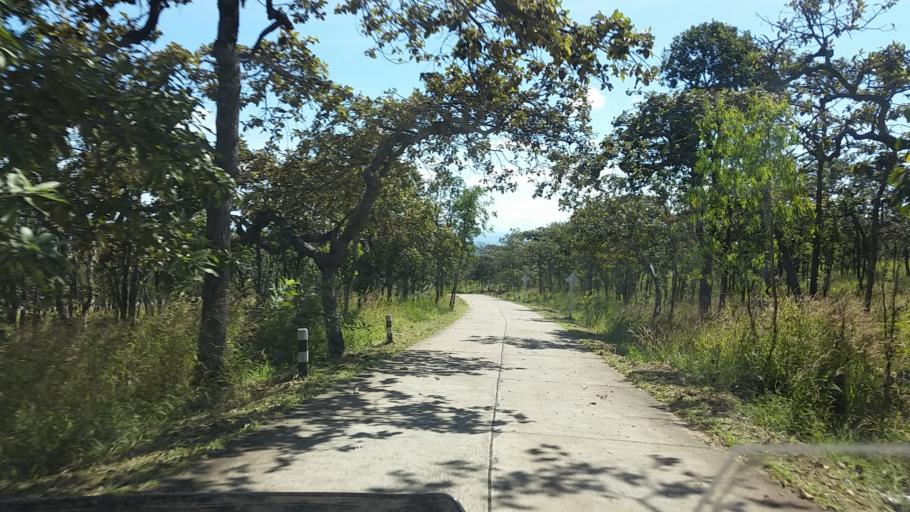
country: TH
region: Chaiyaphum
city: Sap Yai
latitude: 15.6434
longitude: 101.3871
